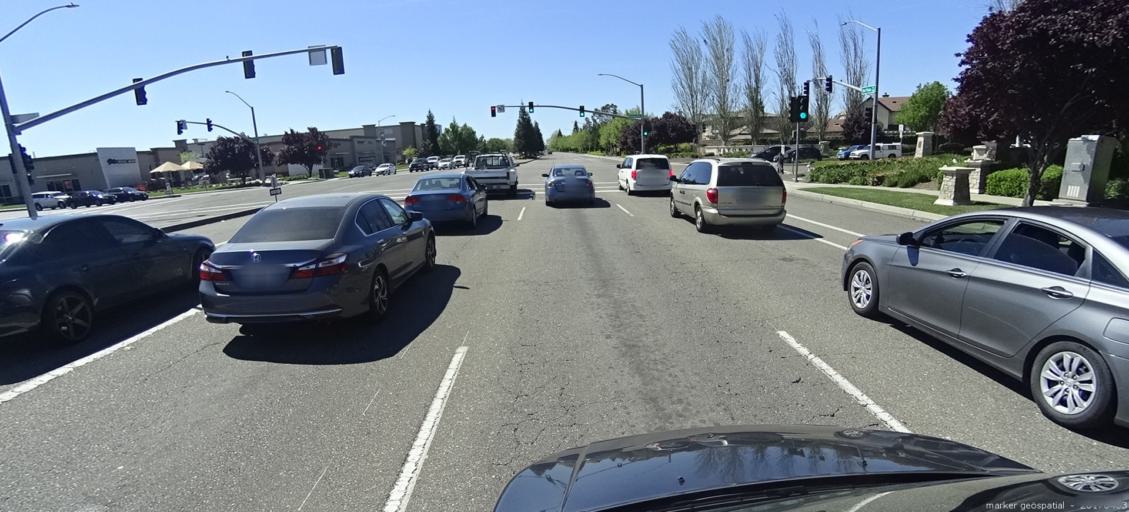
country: US
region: California
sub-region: Sacramento County
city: Rio Linda
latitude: 38.6562
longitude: -121.5022
